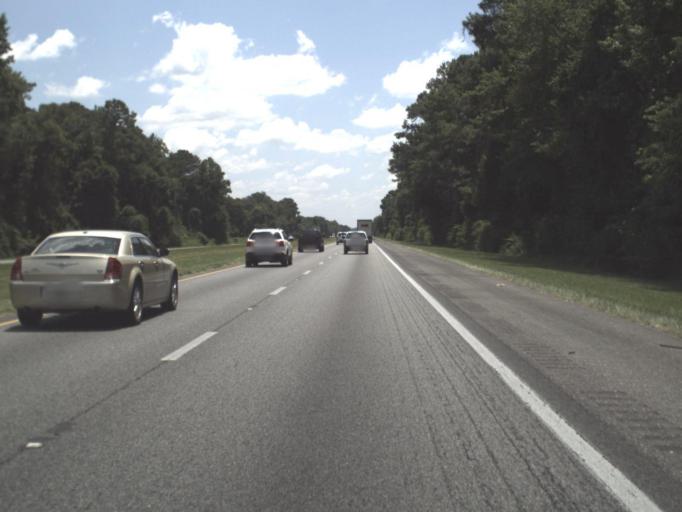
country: US
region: Florida
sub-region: Madison County
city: Madison
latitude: 30.4311
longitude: -83.5991
